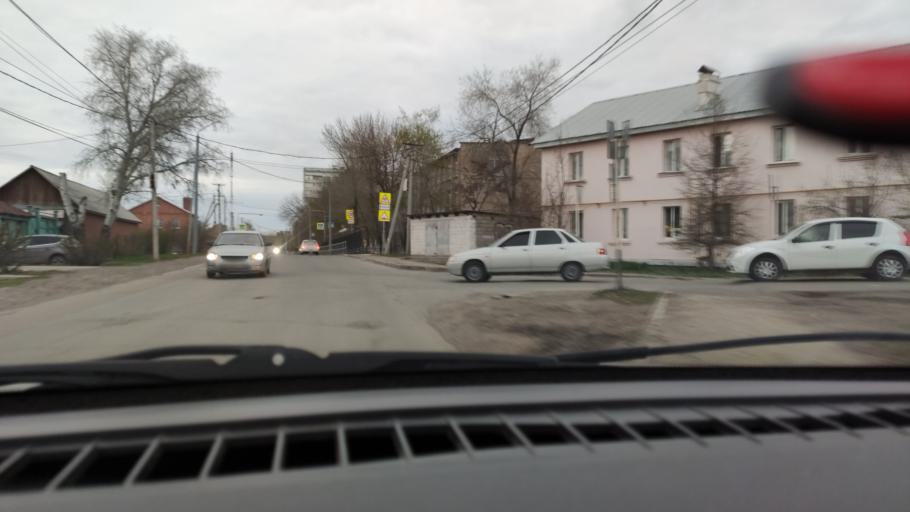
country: RU
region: Orenburg
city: Orenburg
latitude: 51.7777
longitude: 55.1313
